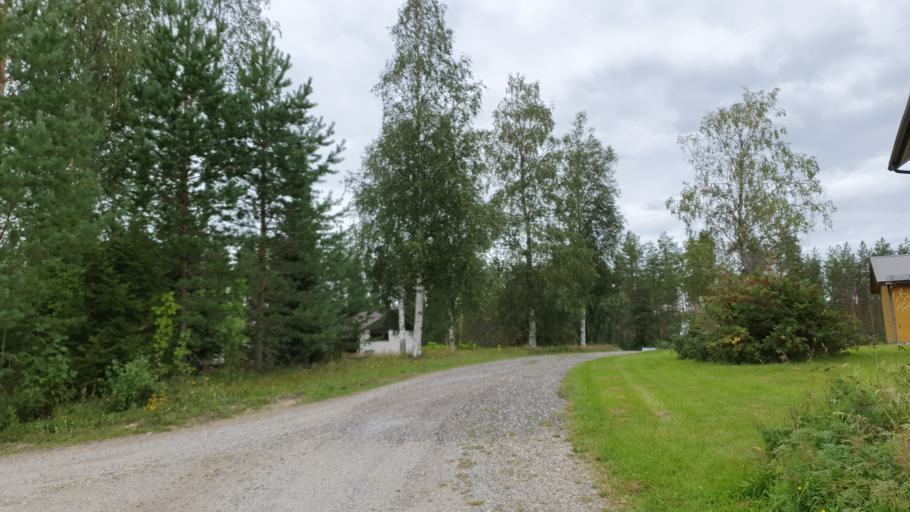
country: FI
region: Kainuu
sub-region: Kehys-Kainuu
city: Kuhmo
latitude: 64.1254
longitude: 29.4591
